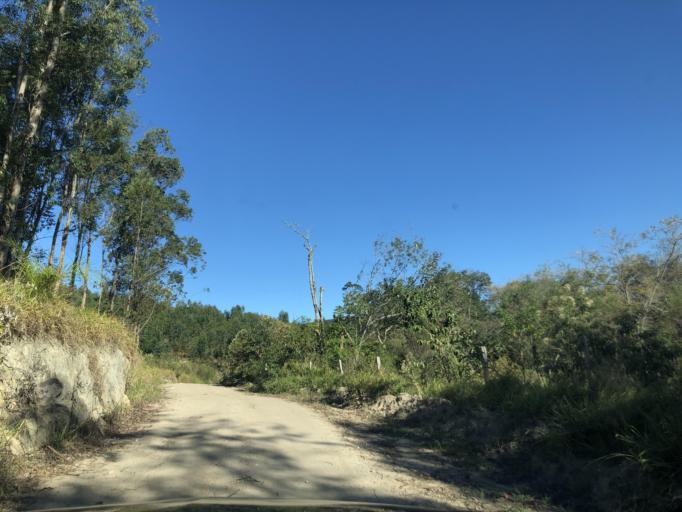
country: BR
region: Sao Paulo
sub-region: Pilar Do Sul
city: Pilar do Sul
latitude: -23.8231
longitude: -47.6279
